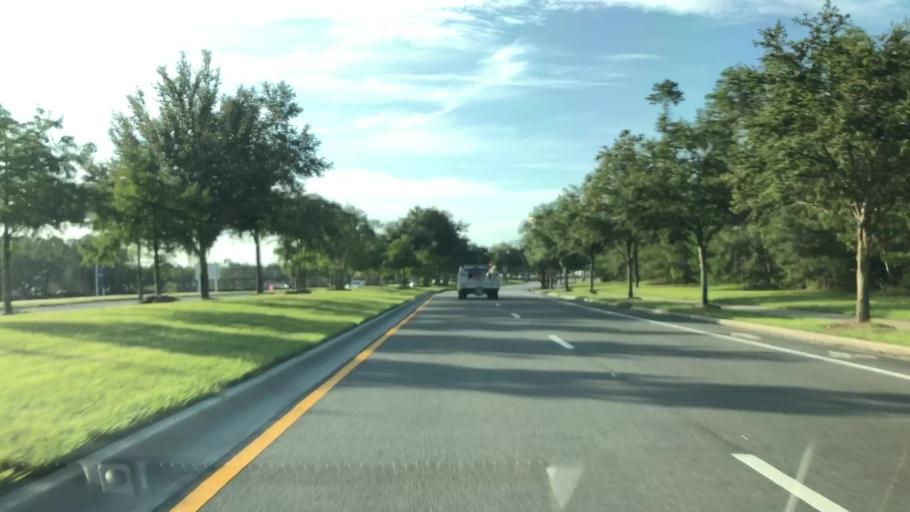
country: US
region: Florida
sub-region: Saint Johns County
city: Palm Valley
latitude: 30.1077
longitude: -81.4444
